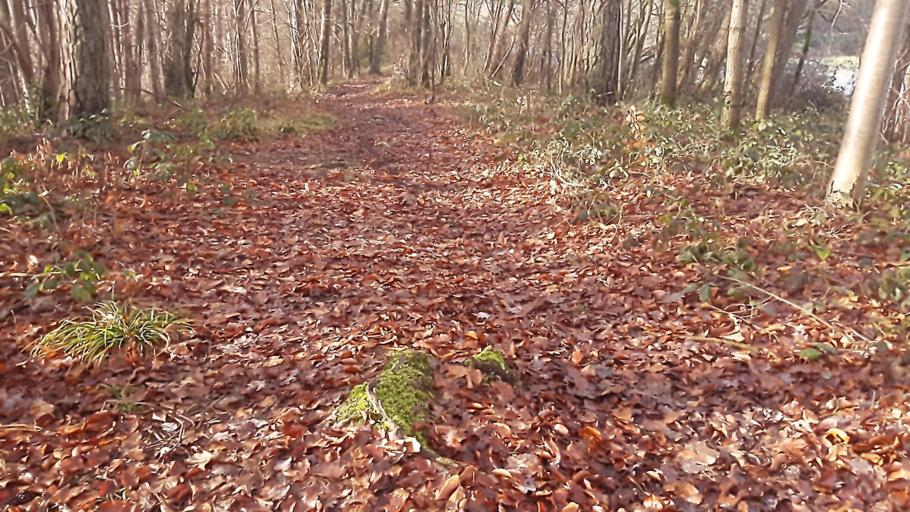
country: FR
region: Champagne-Ardenne
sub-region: Departement des Ardennes
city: Vireux-Molhain
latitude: 50.0782
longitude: 4.6123
